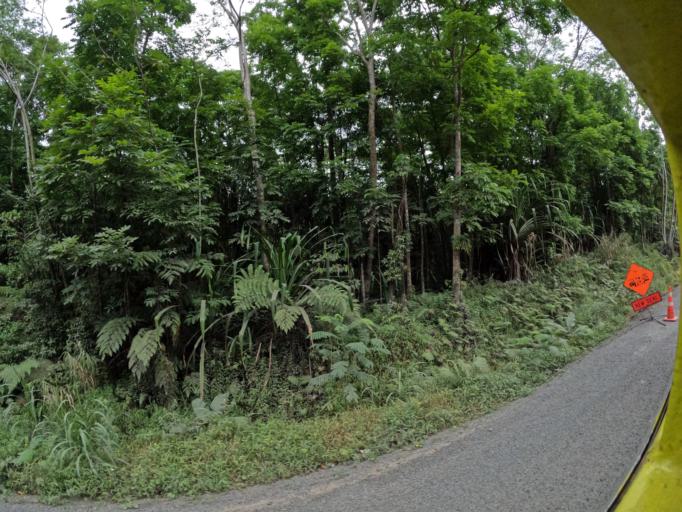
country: FJ
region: Central
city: Suva
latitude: -18.0625
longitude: 178.4568
